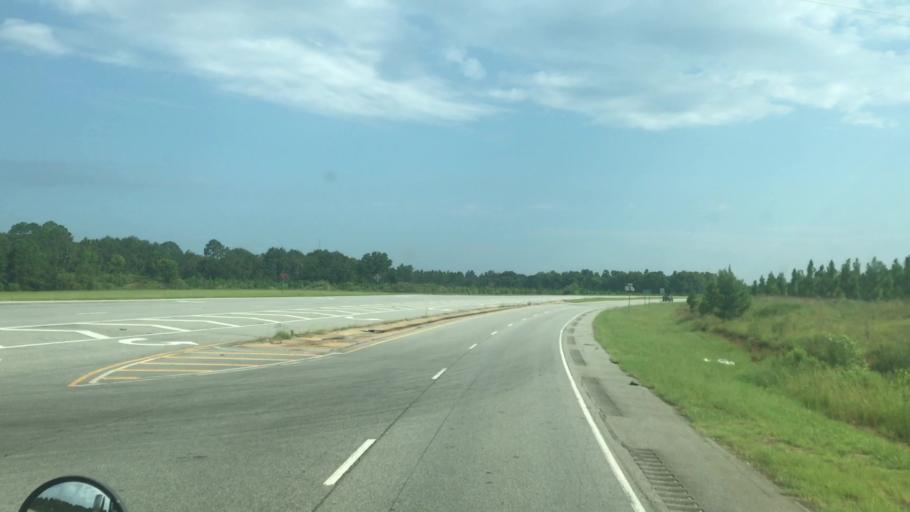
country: US
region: Georgia
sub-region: Early County
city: Blakely
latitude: 31.3580
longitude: -84.9232
